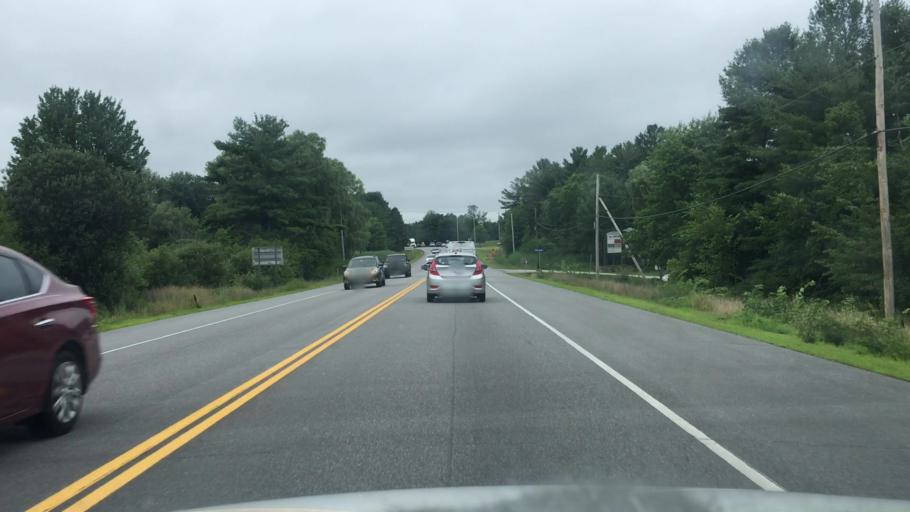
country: US
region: New Hampshire
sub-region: Rockingham County
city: Greenland
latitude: 43.0389
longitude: -70.8347
